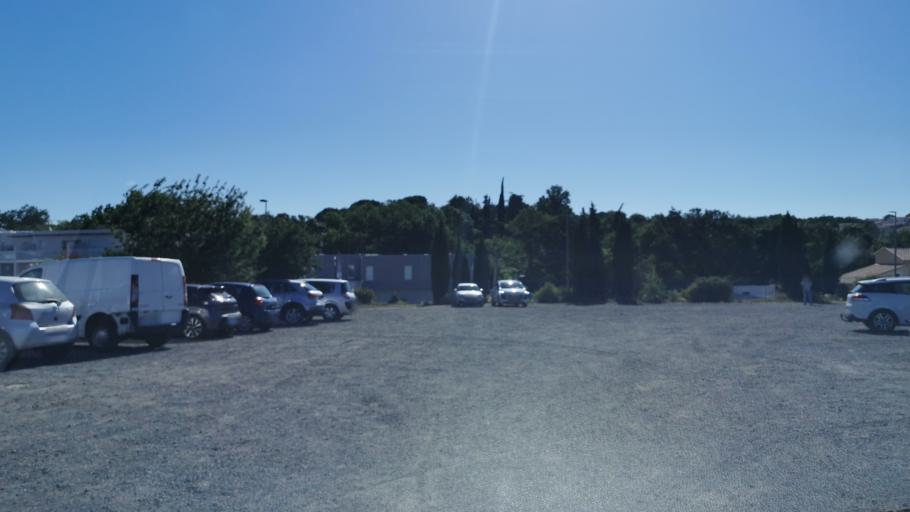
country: FR
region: Languedoc-Roussillon
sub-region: Departement de l'Herault
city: Beziers
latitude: 43.3617
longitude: 3.2114
